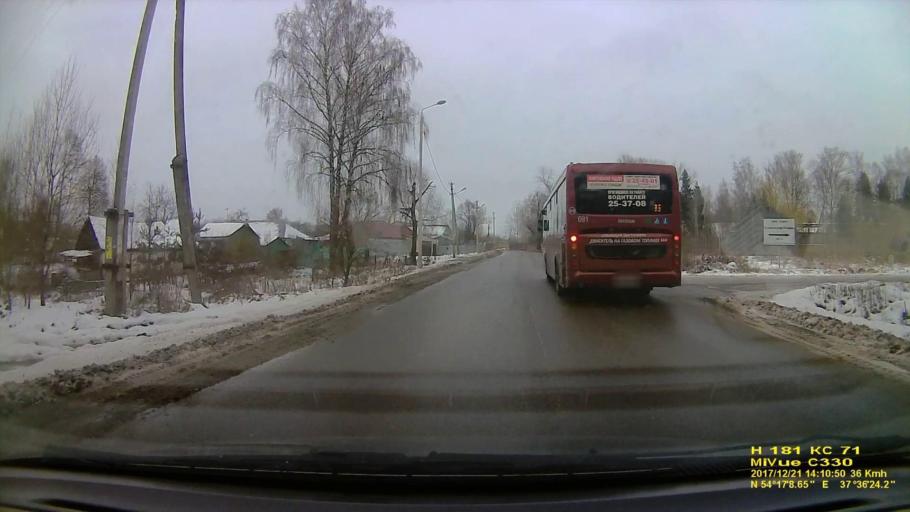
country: RU
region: Tula
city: Gorelki
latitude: 54.2859
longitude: 37.6068
